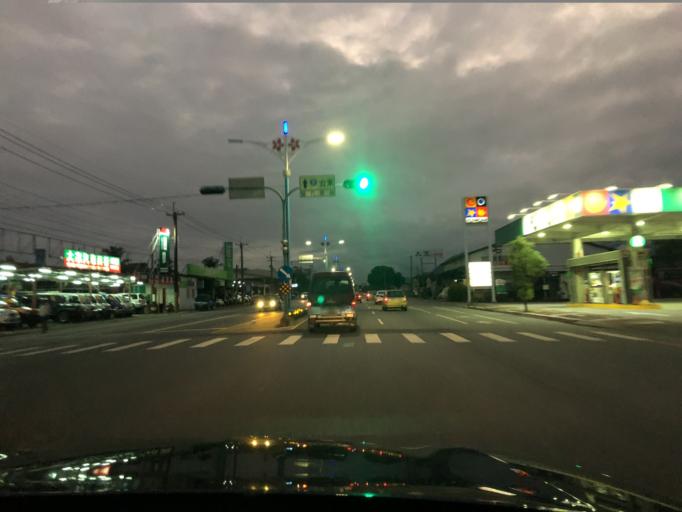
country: TW
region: Taiwan
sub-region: Hualien
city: Hualian
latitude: 23.9709
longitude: 121.5711
